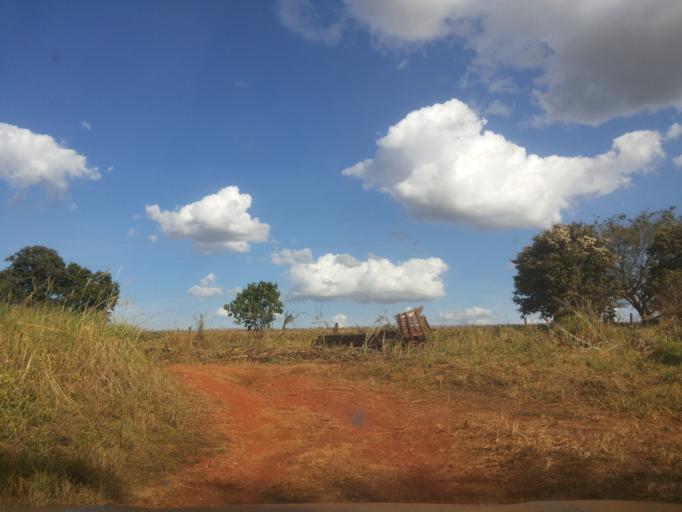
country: BR
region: Minas Gerais
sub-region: Capinopolis
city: Capinopolis
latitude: -18.5865
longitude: -49.4968
